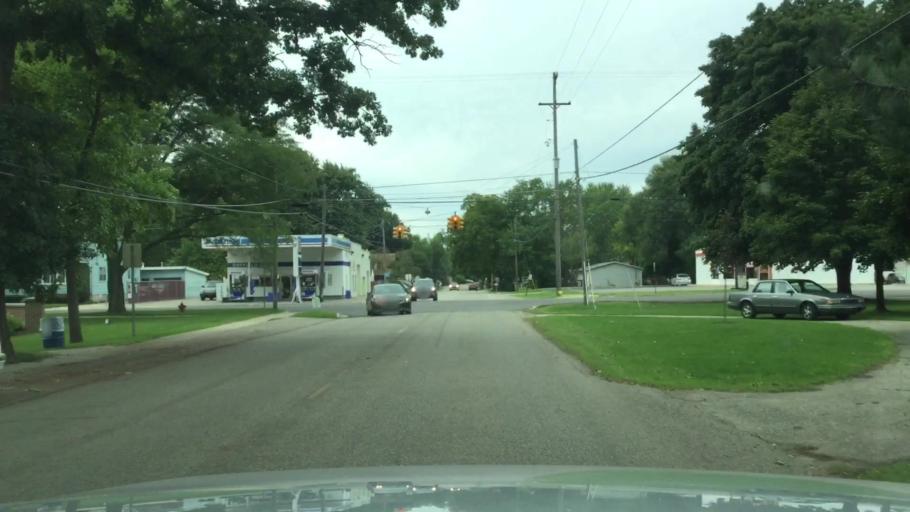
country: US
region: Michigan
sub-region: Shiawassee County
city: Durand
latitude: 42.9181
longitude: -83.9841
